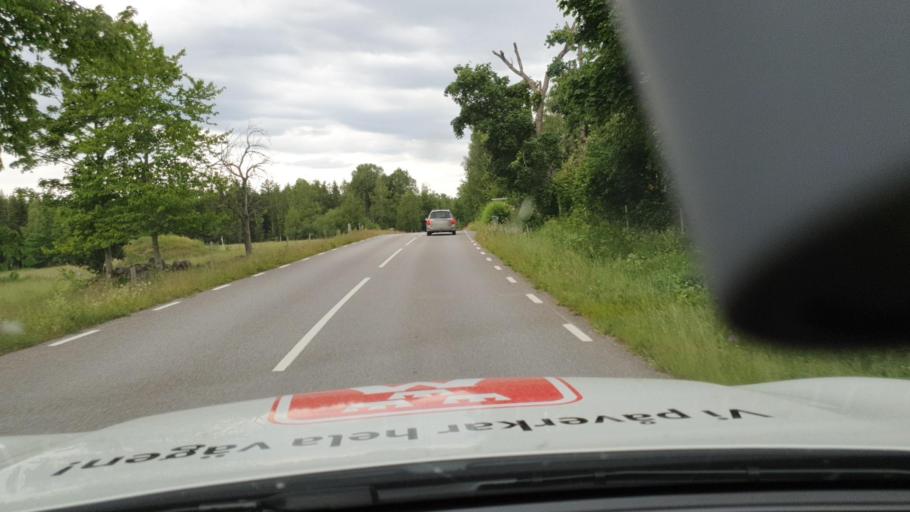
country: SE
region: Vaestra Goetaland
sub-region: Karlsborgs Kommun
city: Karlsborg
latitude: 58.7460
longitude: 14.5057
